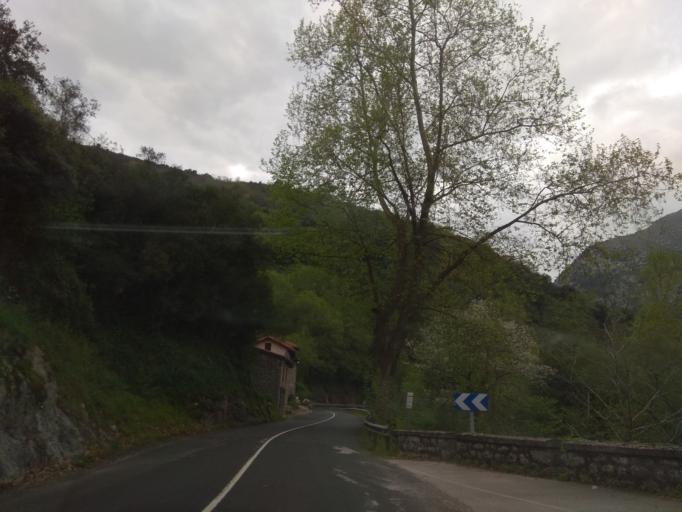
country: ES
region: Cantabria
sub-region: Provincia de Cantabria
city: Tresviso
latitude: 43.3168
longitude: -4.6070
